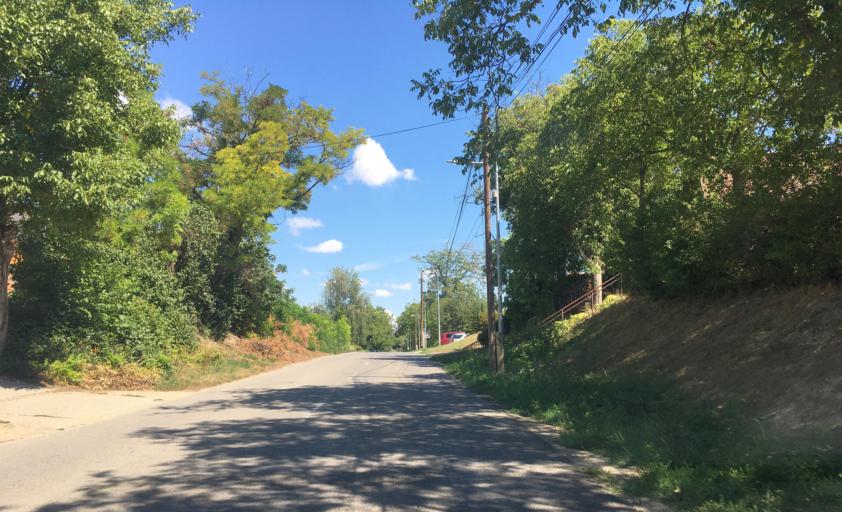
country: HU
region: Komarom-Esztergom
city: Sutto
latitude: 47.8337
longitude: 18.4174
